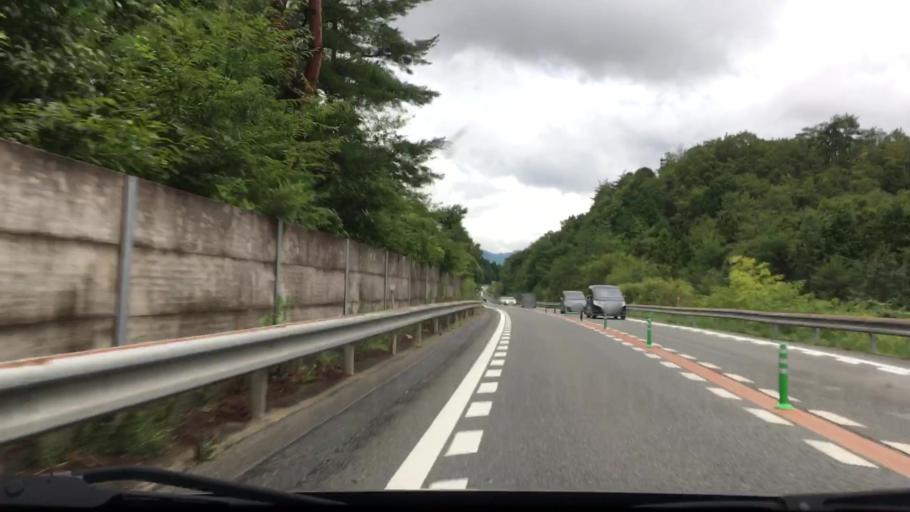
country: JP
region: Hyogo
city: Nishiwaki
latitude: 35.0758
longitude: 134.7707
